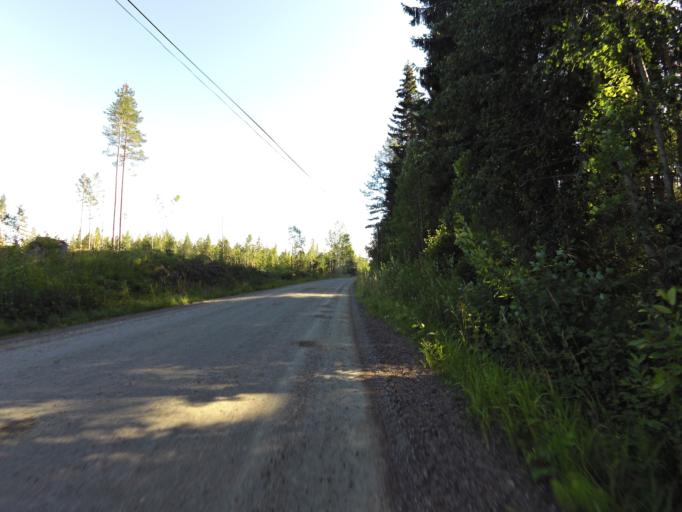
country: SE
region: Gaevleborg
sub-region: Hofors Kommun
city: Hofors
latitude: 60.5802
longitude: 16.2555
